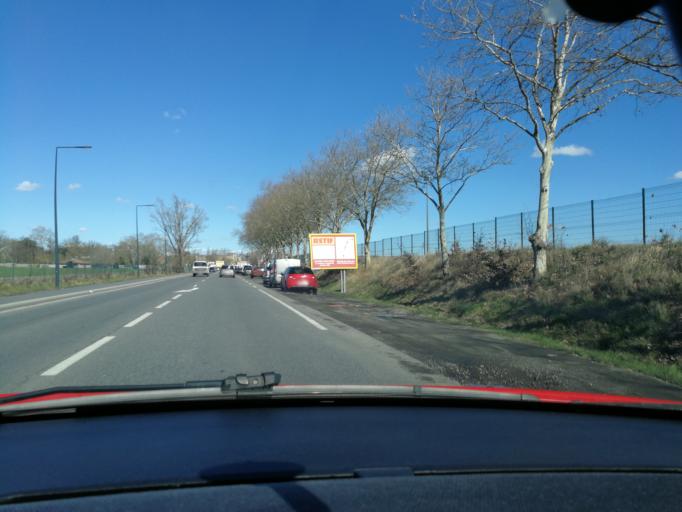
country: FR
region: Midi-Pyrenees
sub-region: Departement de la Haute-Garonne
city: Portet-sur-Garonne
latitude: 43.5392
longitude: 1.3890
